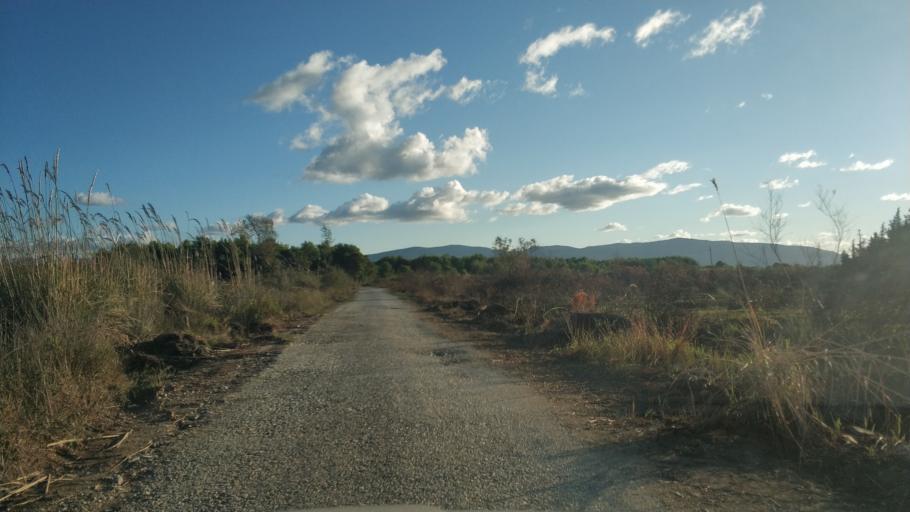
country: AL
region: Vlore
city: Vlore
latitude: 40.5072
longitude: 19.4233
